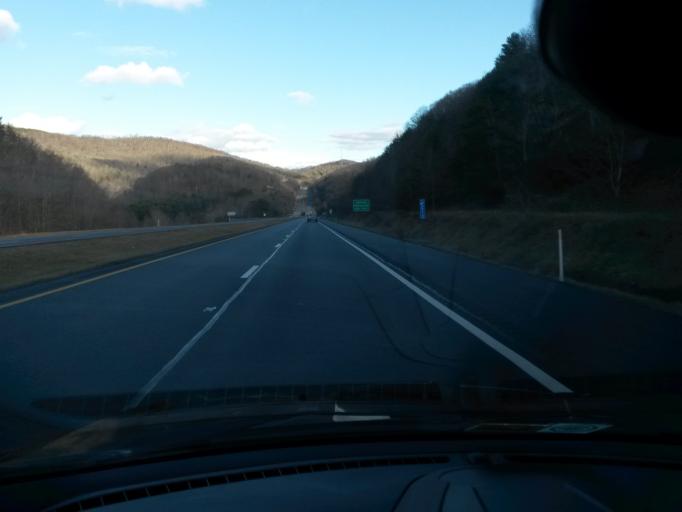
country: US
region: West Virginia
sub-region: Mercer County
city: Athens
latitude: 37.3403
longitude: -80.9658
